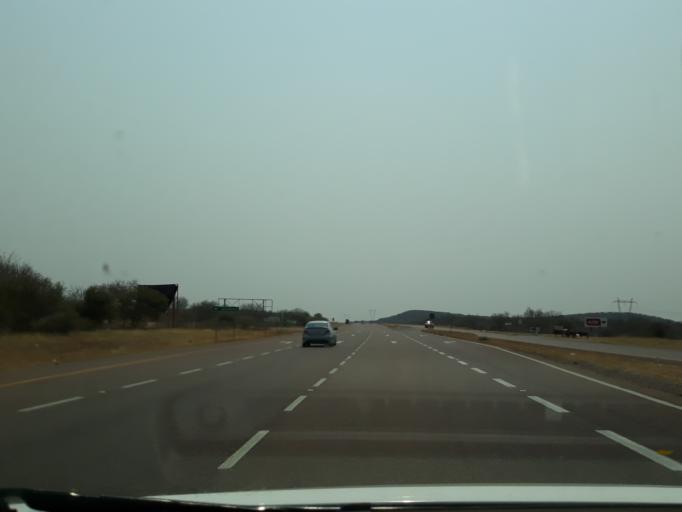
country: BW
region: Kgatleng
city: Bokaa
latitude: -24.4036
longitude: 26.0553
